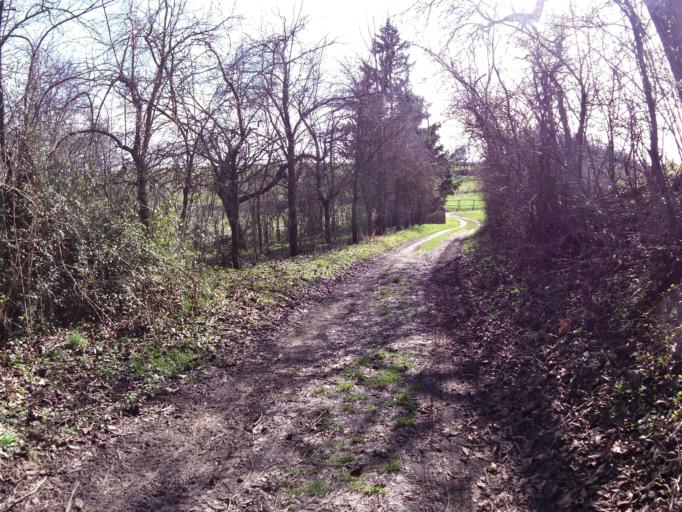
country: DE
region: Bavaria
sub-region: Regierungsbezirk Unterfranken
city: Buchbrunn
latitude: 49.7469
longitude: 10.1239
